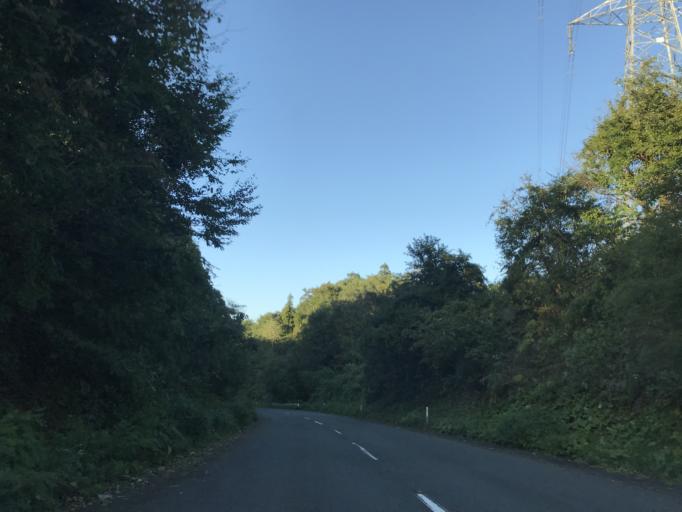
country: JP
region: Iwate
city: Ichinoseki
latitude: 38.9871
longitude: 141.0447
